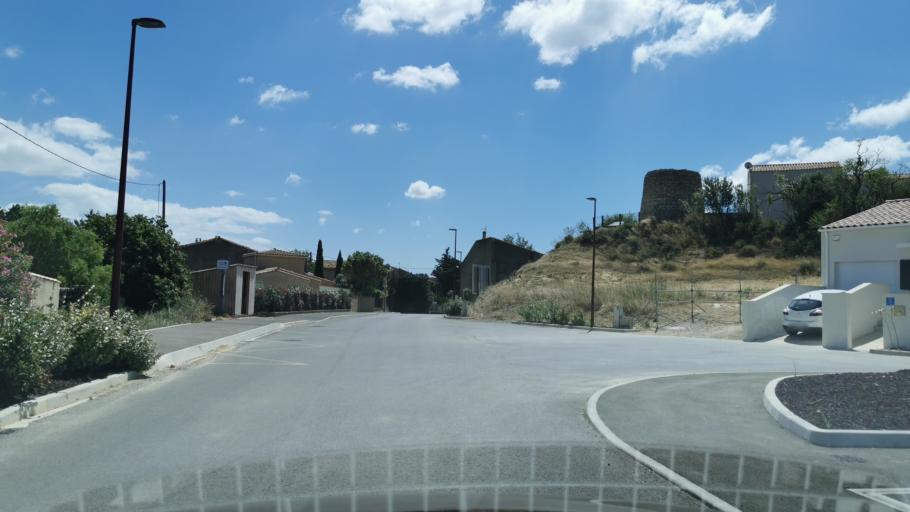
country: FR
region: Languedoc-Roussillon
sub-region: Departement de l'Aude
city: Peyriac-de-Mer
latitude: 43.0900
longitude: 2.9583
